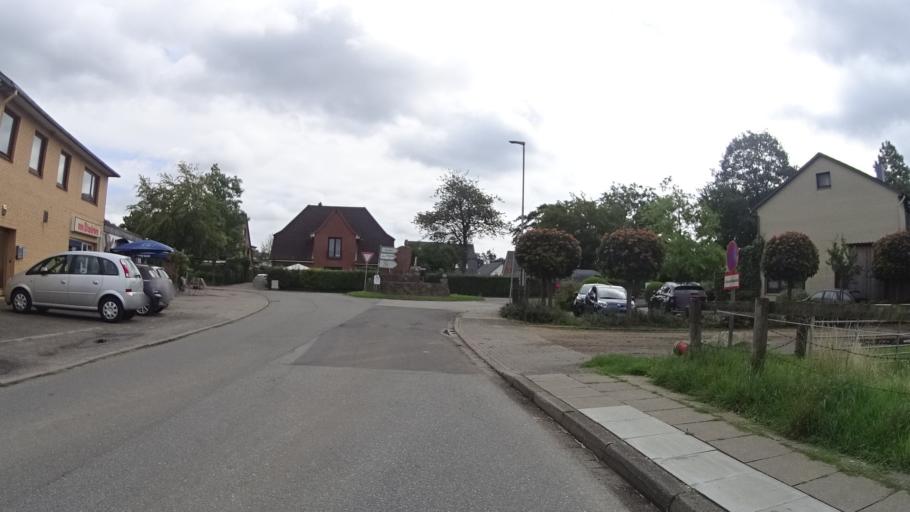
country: DE
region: Schleswig-Holstein
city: Tangstedt
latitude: 53.7491
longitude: 10.0663
